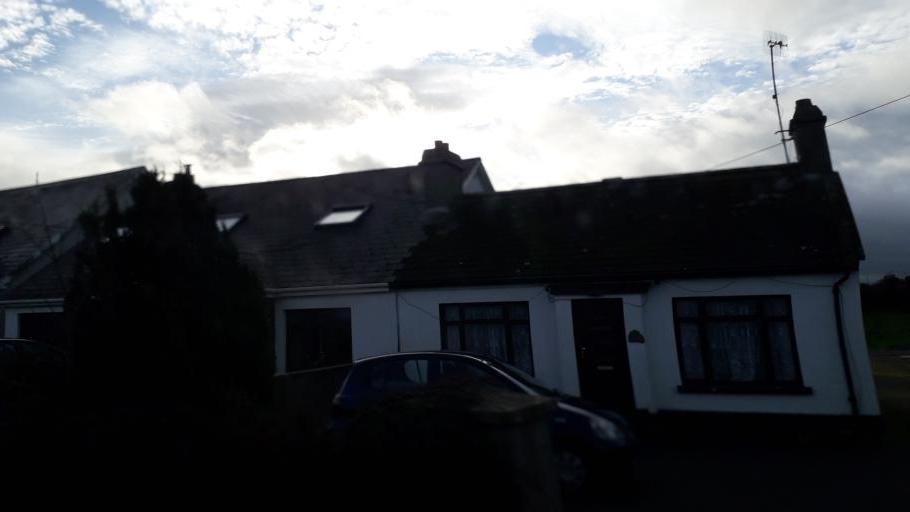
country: IE
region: Leinster
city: Balrothery
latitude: 53.5789
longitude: -6.1590
